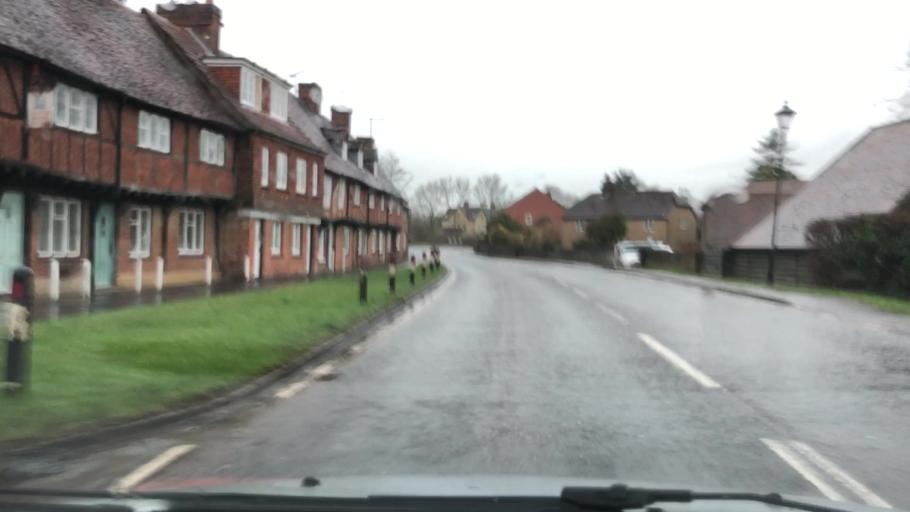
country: GB
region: England
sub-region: Hampshire
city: Odiham
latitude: 51.2624
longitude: -0.9524
